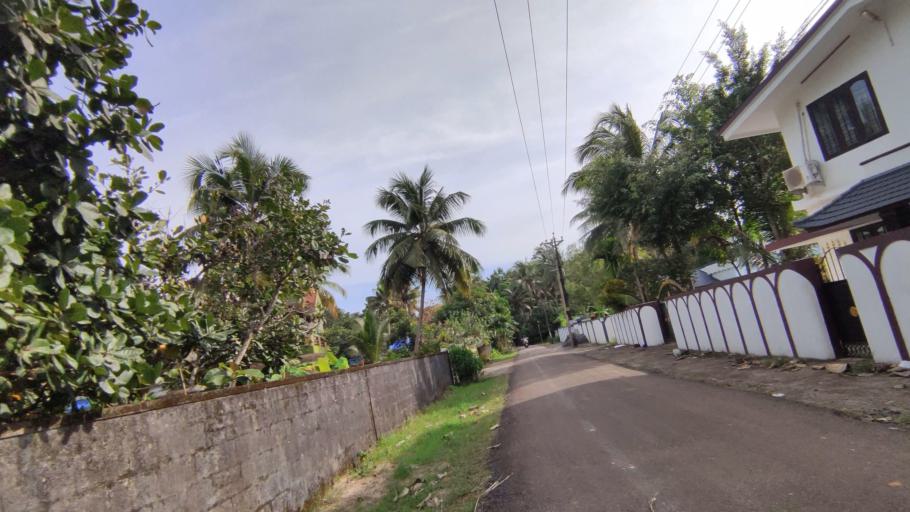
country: IN
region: Kerala
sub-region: Alappuzha
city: Shertallai
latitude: 9.6392
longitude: 76.3383
